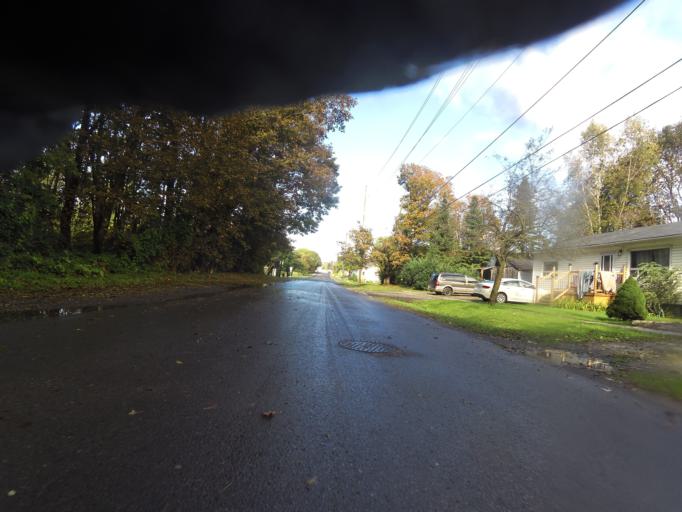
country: CA
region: Ontario
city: Cobourg
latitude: 43.9479
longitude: -78.3065
